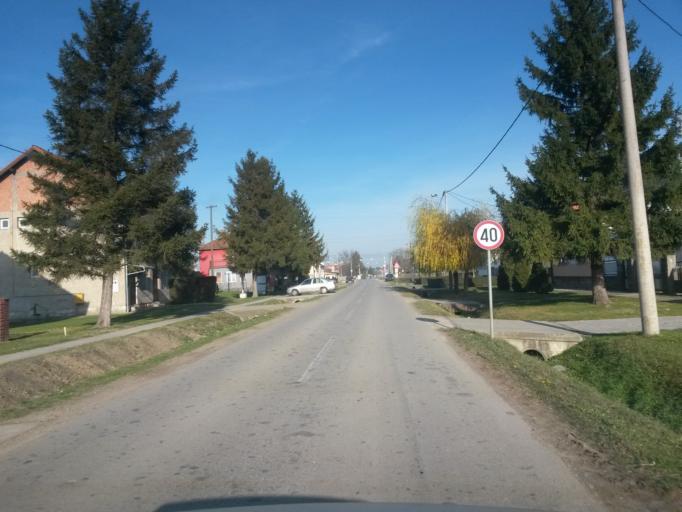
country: HR
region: Vukovarsko-Srijemska
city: Slakovci
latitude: 45.2450
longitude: 18.9005
